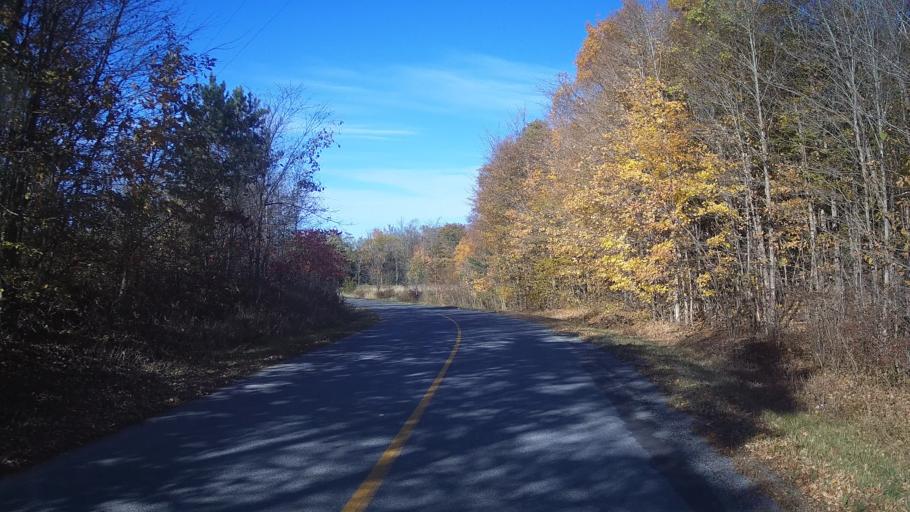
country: CA
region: Ontario
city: Kingston
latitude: 44.4613
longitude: -76.5009
